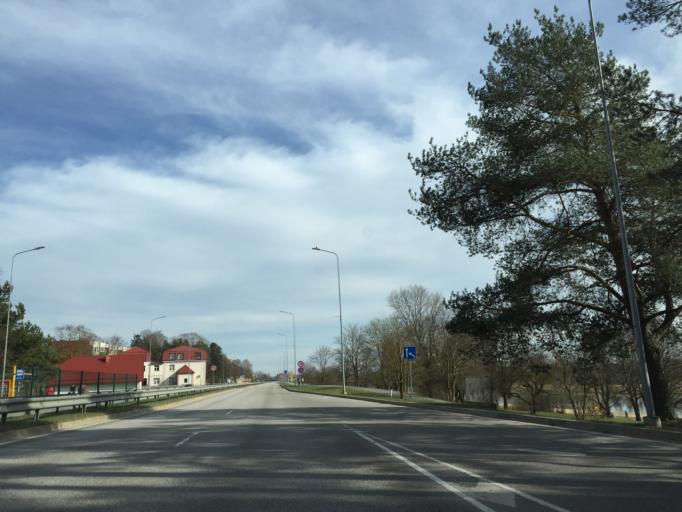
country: LV
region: Ogre
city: Ogre
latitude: 56.8152
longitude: 24.5915
